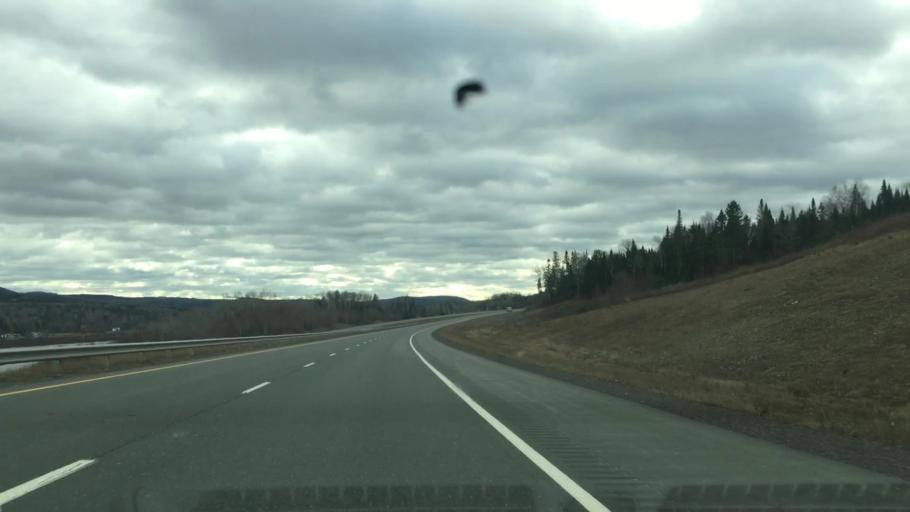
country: US
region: Maine
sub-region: Aroostook County
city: Fort Fairfield
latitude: 46.6785
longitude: -67.7308
